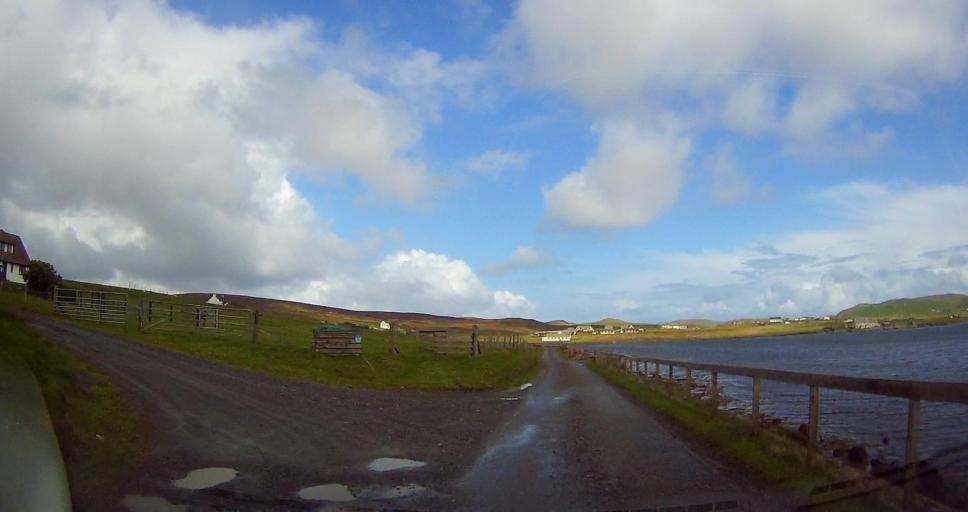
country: GB
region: Scotland
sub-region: Shetland Islands
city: Lerwick
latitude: 60.5804
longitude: -1.3331
